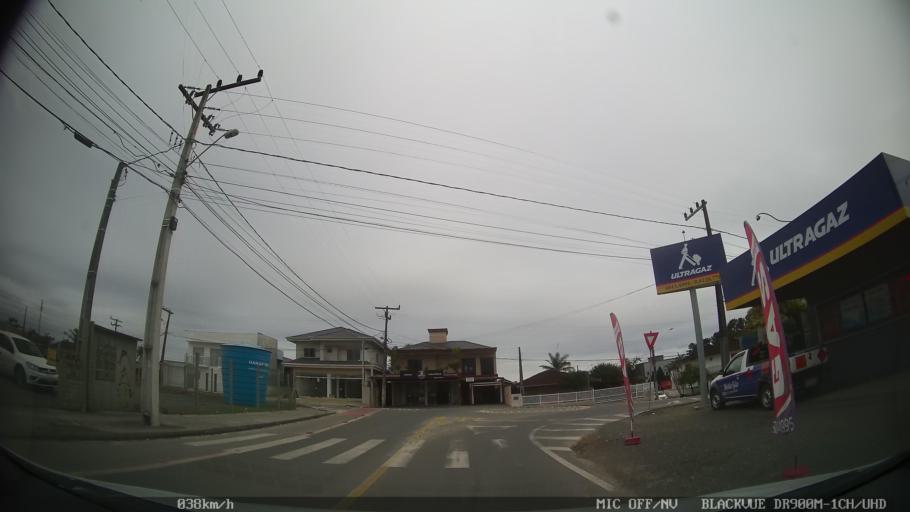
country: BR
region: Santa Catarina
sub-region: Joinville
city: Joinville
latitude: -26.2881
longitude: -48.9098
